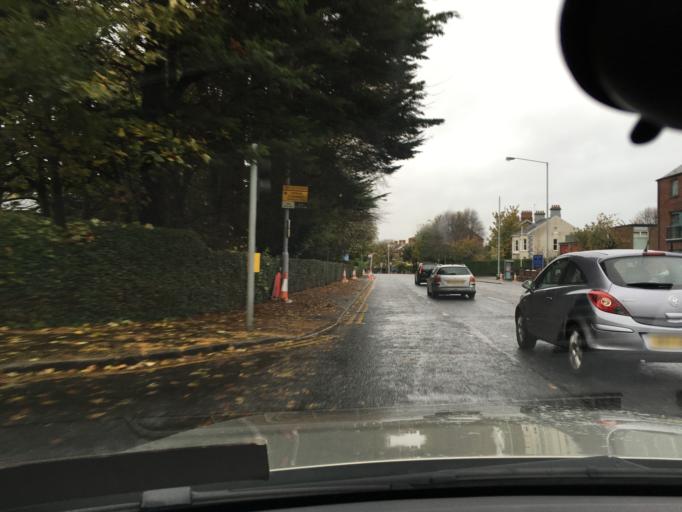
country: GB
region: Northern Ireland
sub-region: Castlereagh District
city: Castlereagh
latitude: 54.5958
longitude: -5.8752
